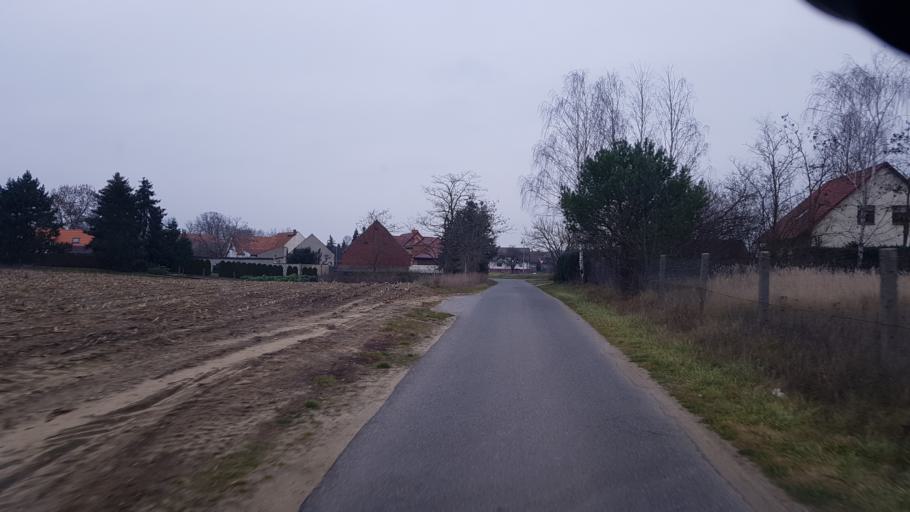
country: DE
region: Brandenburg
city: Schenkendobern
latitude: 51.9347
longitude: 14.5630
